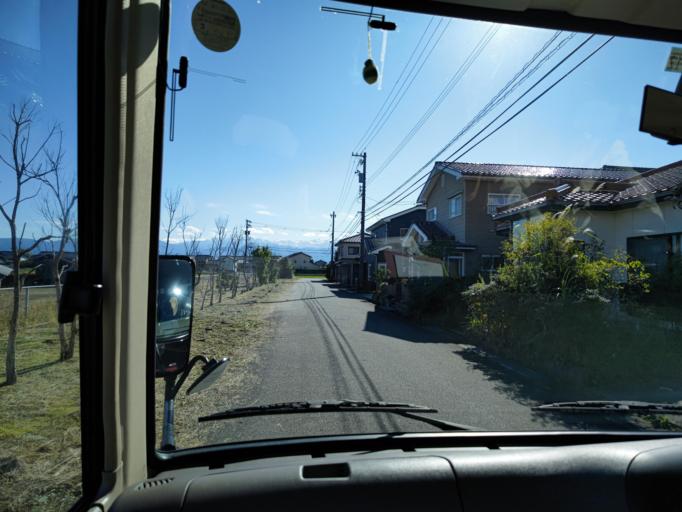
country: JP
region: Toyama
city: Nyuzen
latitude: 36.9103
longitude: 137.4280
